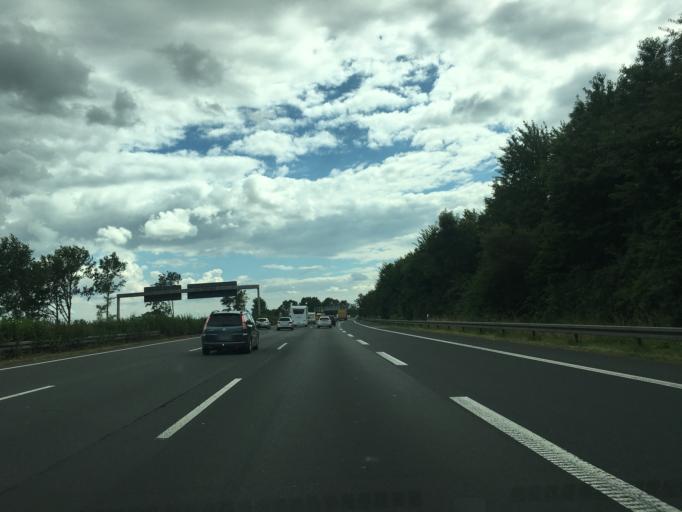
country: DE
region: North Rhine-Westphalia
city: Kamen
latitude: 51.5925
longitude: 7.6850
